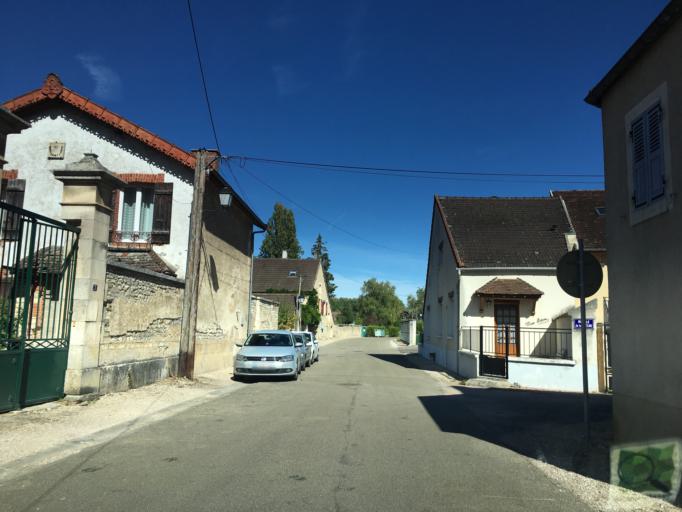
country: FR
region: Bourgogne
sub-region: Departement de l'Yonne
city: Vermenton
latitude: 47.6006
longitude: 3.6813
